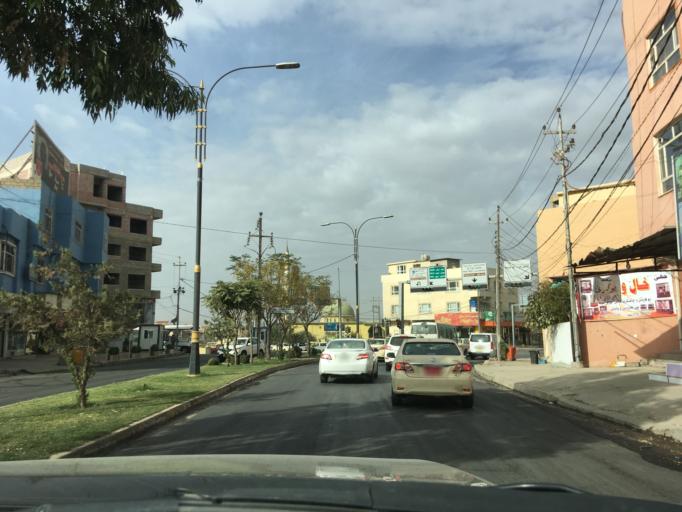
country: IQ
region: Dahuk
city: Dihok
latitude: 36.8502
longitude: 42.9862
